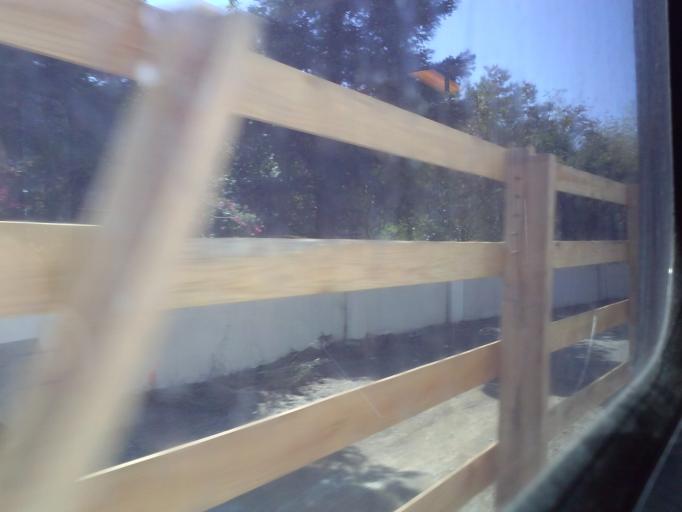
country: US
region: California
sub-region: Santa Clara County
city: Mountain View
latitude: 37.3899
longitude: -122.0605
